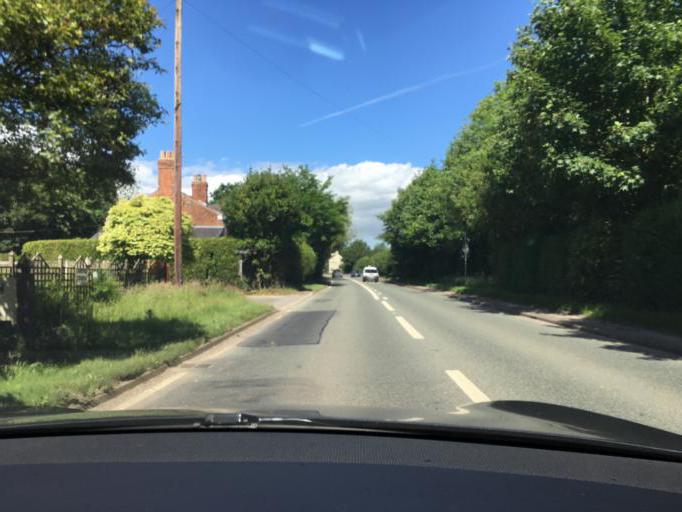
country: GB
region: England
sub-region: Cheshire East
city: Mobberley
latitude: 53.2876
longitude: -2.3371
